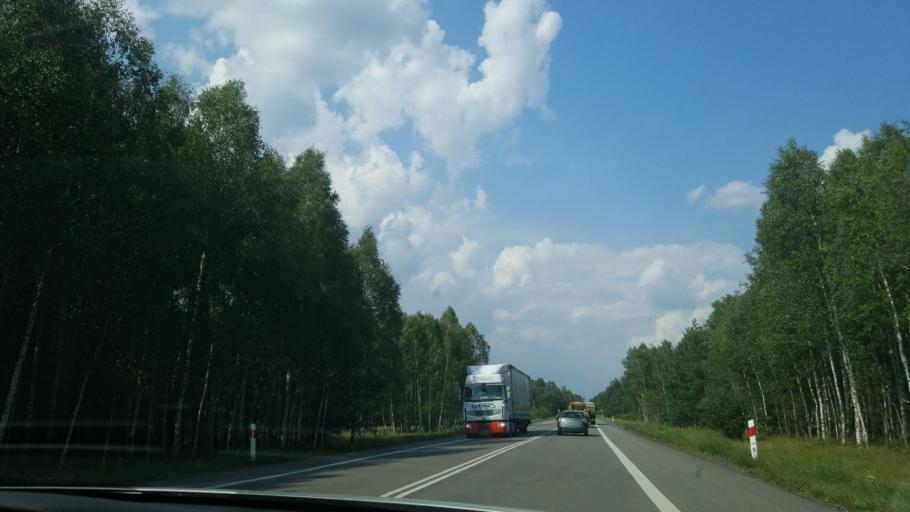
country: PL
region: Subcarpathian Voivodeship
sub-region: Powiat nizanski
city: Jarocin
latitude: 50.6246
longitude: 22.2866
